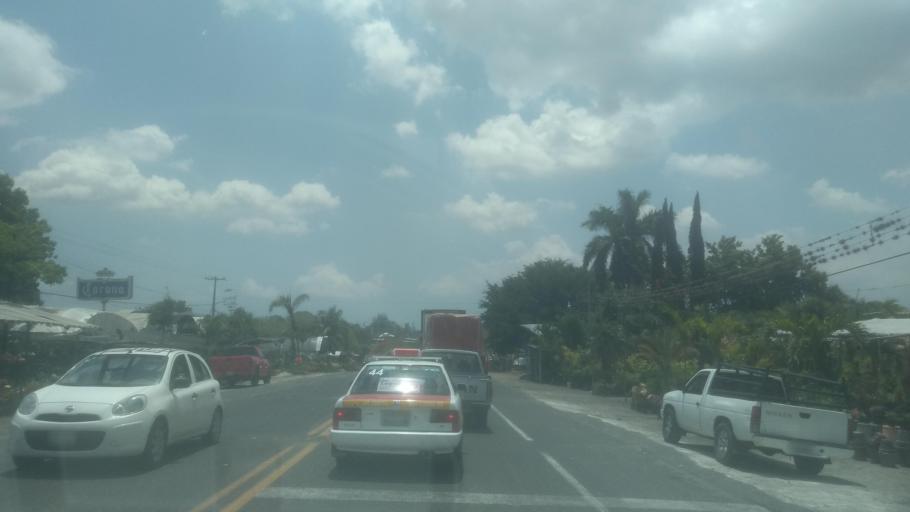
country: MX
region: Veracruz
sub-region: Emiliano Zapata
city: Plan del Rio
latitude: 19.3919
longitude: -96.6339
